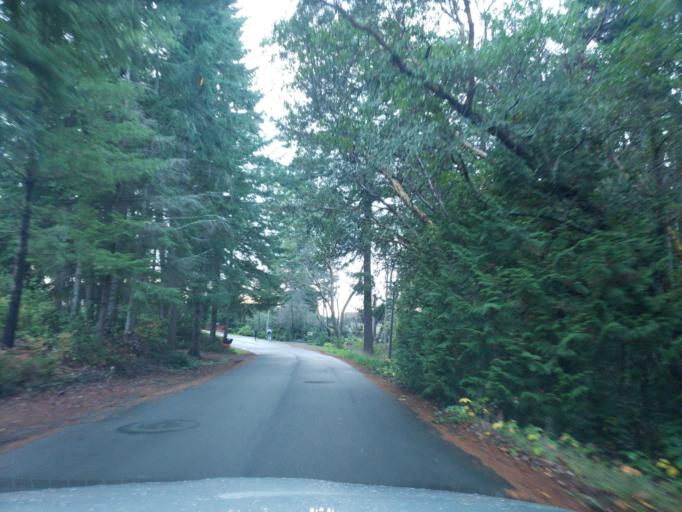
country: US
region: Washington
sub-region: Snohomish County
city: Woodway
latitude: 47.7667
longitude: -122.3793
